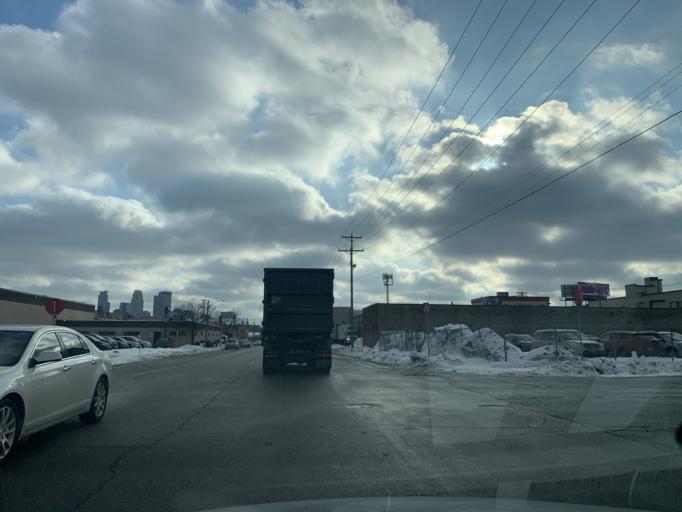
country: US
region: Minnesota
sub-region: Hennepin County
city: Minneapolis
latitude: 45.0016
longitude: -93.2802
